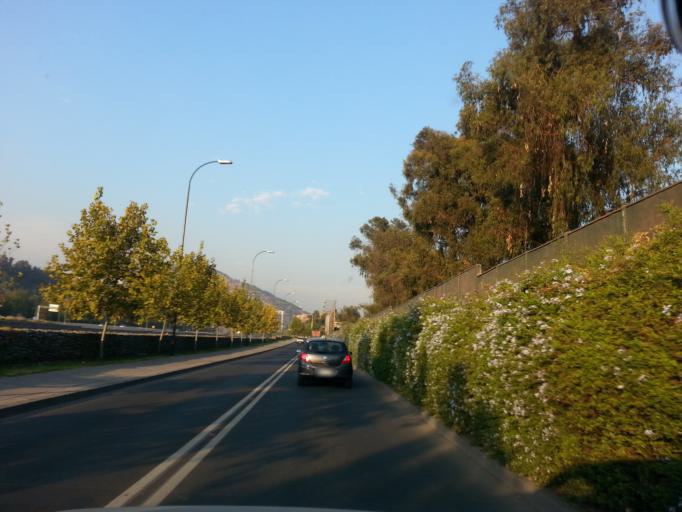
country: CL
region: Santiago Metropolitan
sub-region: Provincia de Santiago
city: Villa Presidente Frei, Nunoa, Santiago, Chile
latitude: -33.3773
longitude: -70.5602
